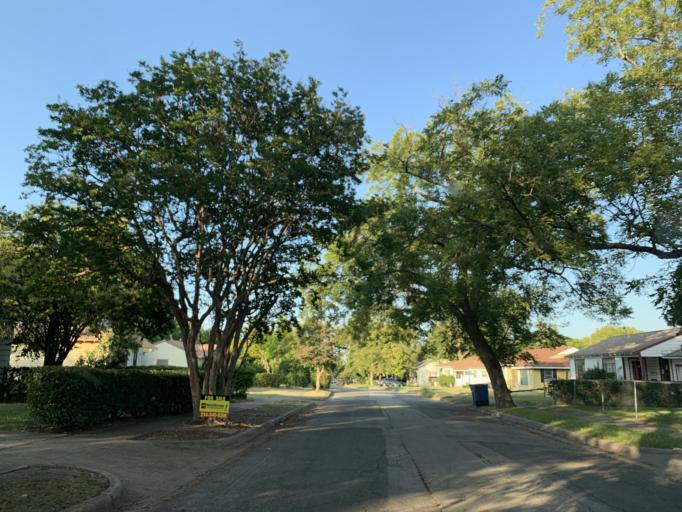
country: US
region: Texas
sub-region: Dallas County
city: Dallas
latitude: 32.7050
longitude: -96.7873
